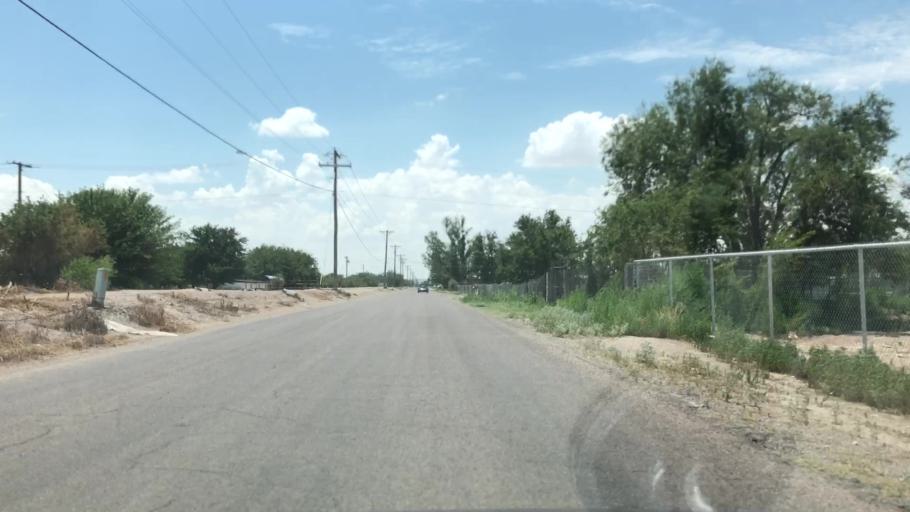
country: US
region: Texas
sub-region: El Paso County
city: Canutillo
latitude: 31.9158
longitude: -106.6248
